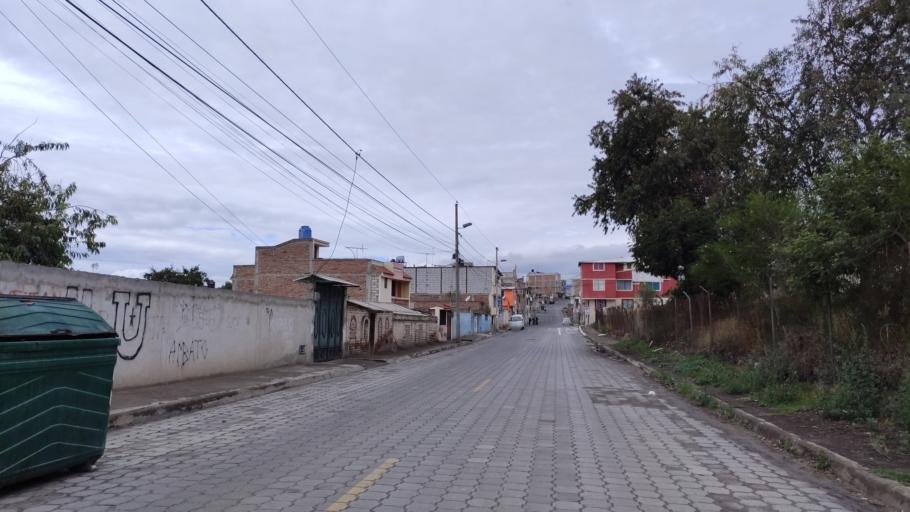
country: EC
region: Chimborazo
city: Riobamba
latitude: -1.6548
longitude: -78.6416
